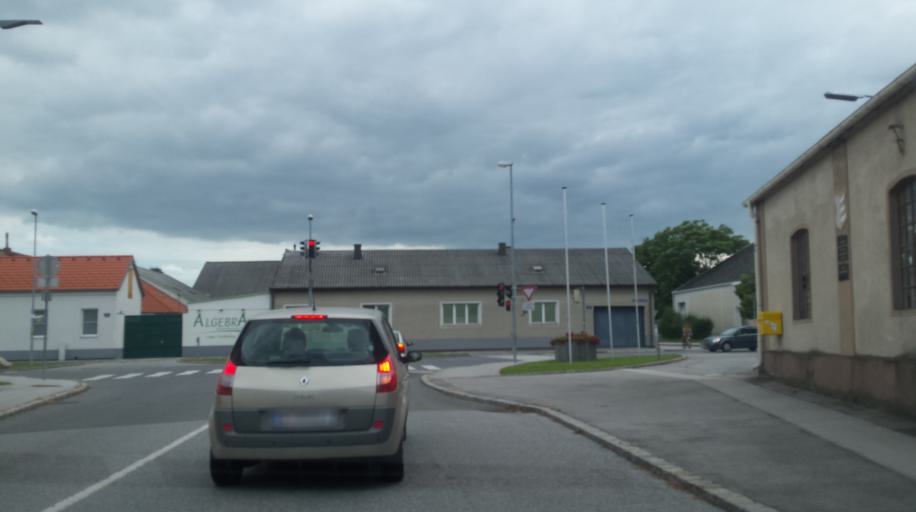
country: AT
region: Lower Austria
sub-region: Politischer Bezirk Wien-Umgebung
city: Zwolfaxing
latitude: 48.1103
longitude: 16.4620
